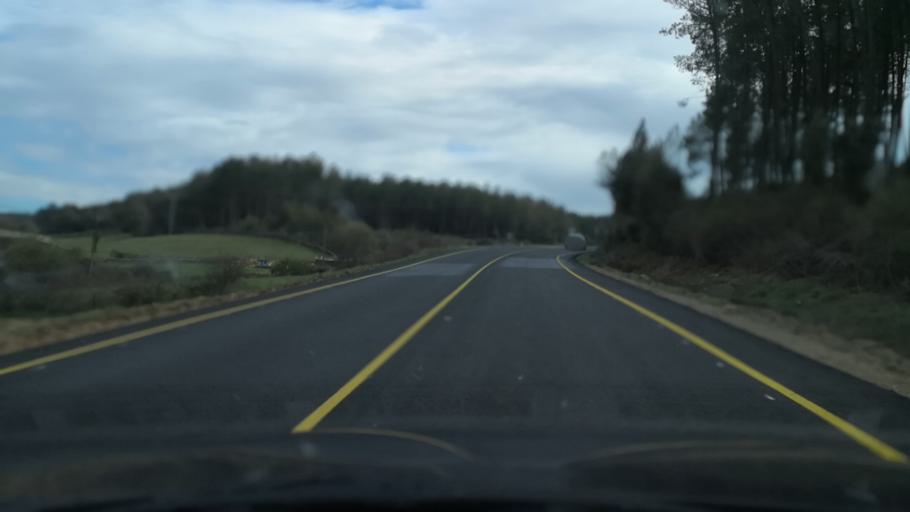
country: ES
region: Castille and Leon
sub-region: Provincia de Salamanca
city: Robleda
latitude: 40.3814
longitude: -6.6109
